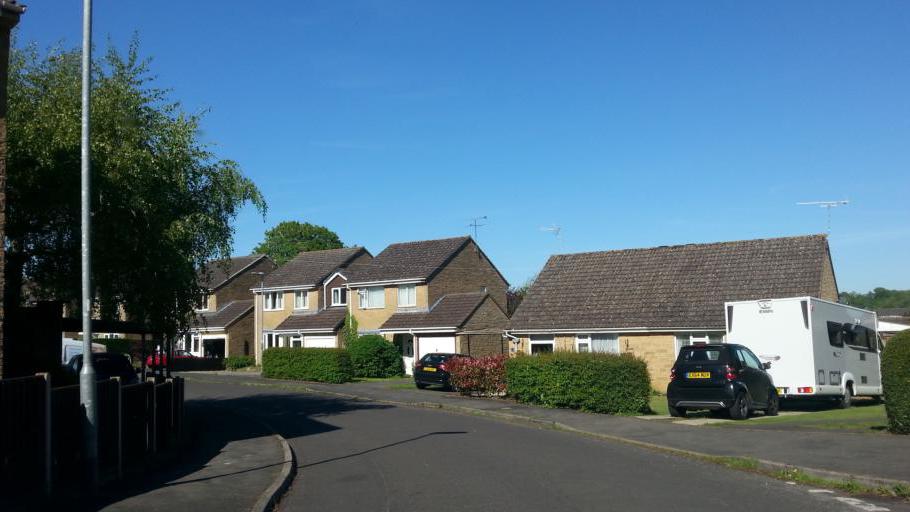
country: GB
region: England
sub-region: Somerset
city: Milborne Port
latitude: 50.9671
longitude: -2.4670
